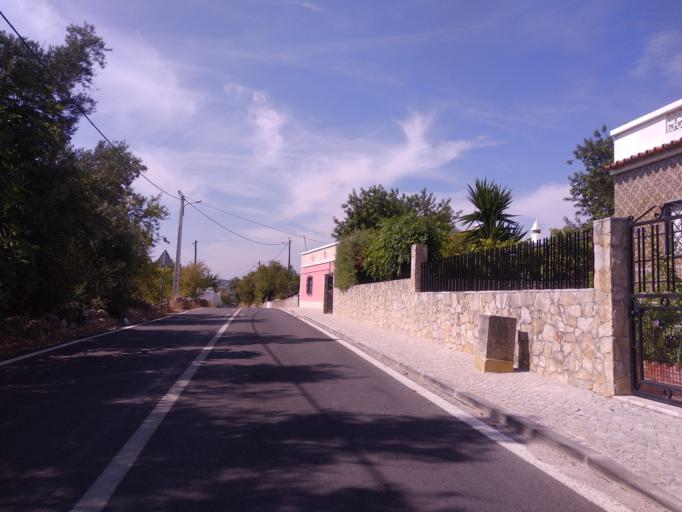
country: PT
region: Faro
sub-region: Faro
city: Santa Barbara de Nexe
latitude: 37.1333
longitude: -7.9550
